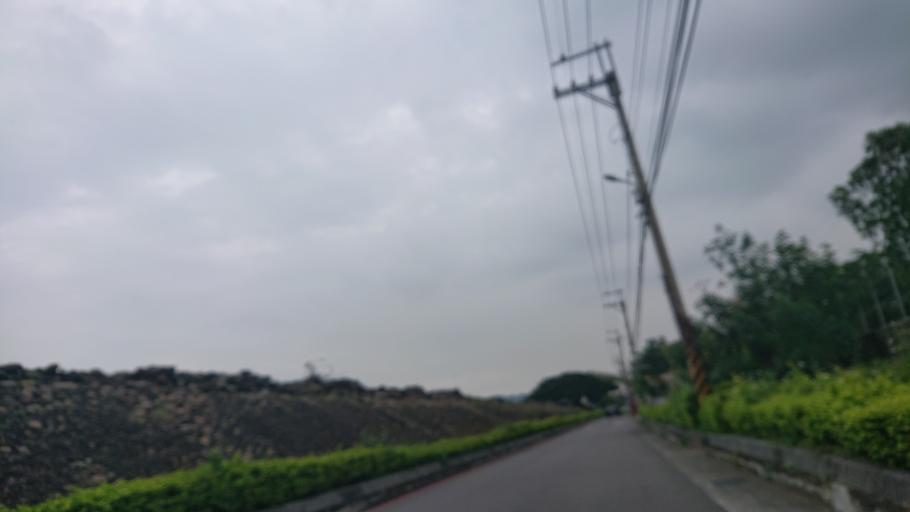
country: TW
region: Taiwan
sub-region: Taoyuan
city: Taoyuan
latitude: 24.9385
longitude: 121.3530
